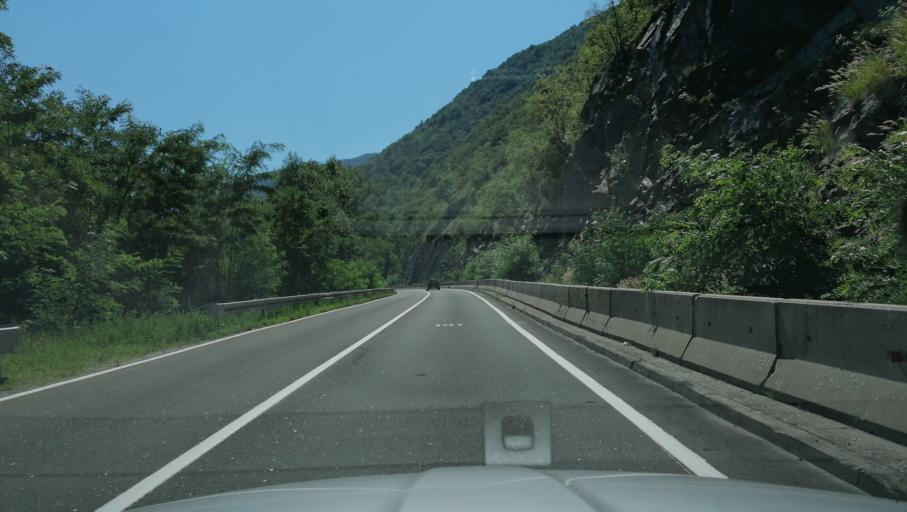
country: RS
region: Central Serbia
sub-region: Raski Okrug
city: Kraljevo
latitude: 43.6097
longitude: 20.5535
